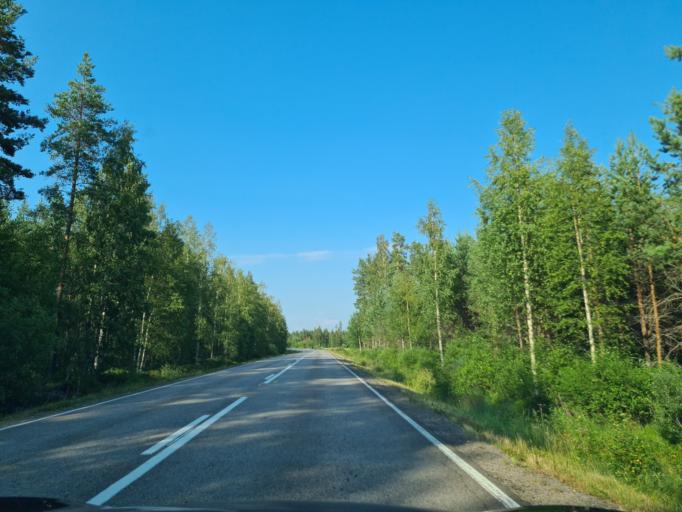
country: FI
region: Satakunta
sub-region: Pohjois-Satakunta
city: Karvia
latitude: 62.3106
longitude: 22.6525
